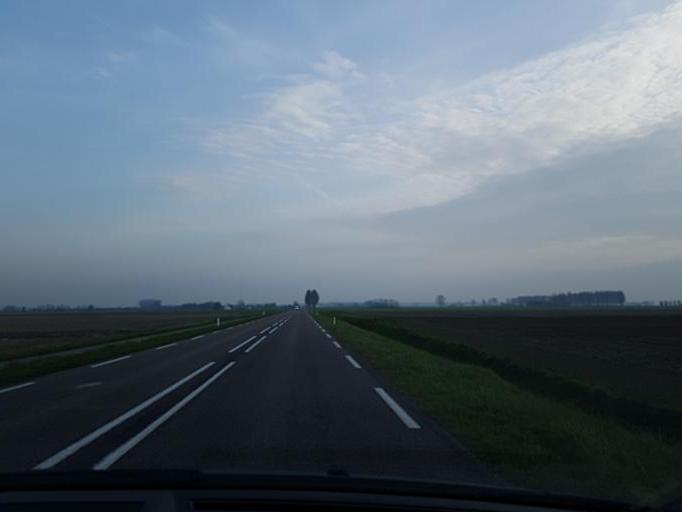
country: NL
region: Zeeland
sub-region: Gemeente Hulst
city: Hulst
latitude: 51.3287
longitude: 4.0334
